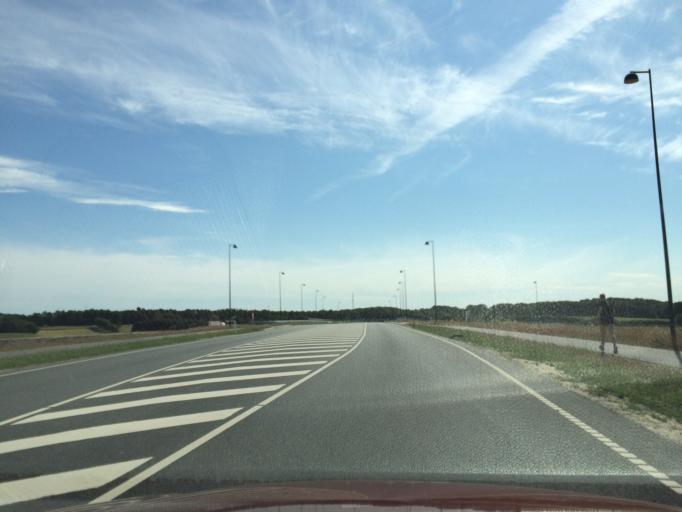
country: DK
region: Central Jutland
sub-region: Silkeborg Kommune
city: Silkeborg
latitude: 56.2024
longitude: 9.5528
